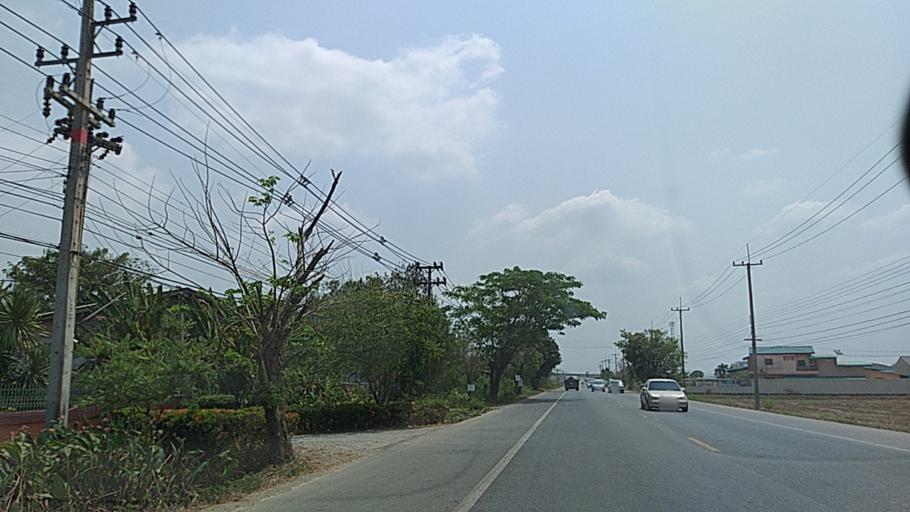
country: TH
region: Chachoengsao
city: Chachoengsao
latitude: 13.7525
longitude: 101.0766
